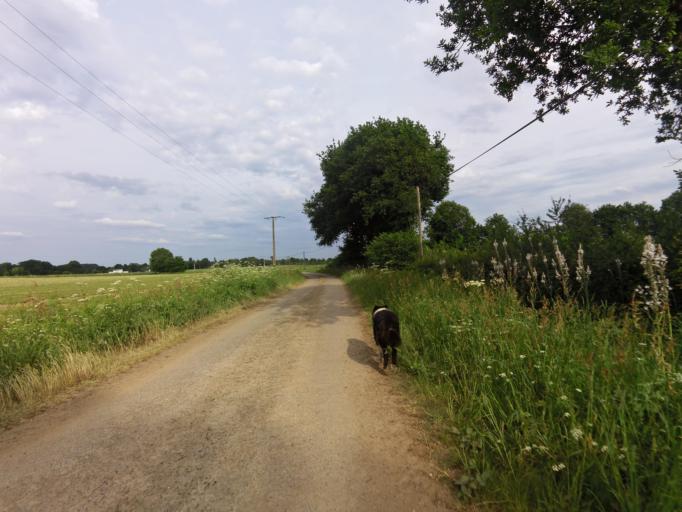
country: FR
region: Brittany
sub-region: Departement du Morbihan
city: Molac
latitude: 47.7682
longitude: -2.4275
